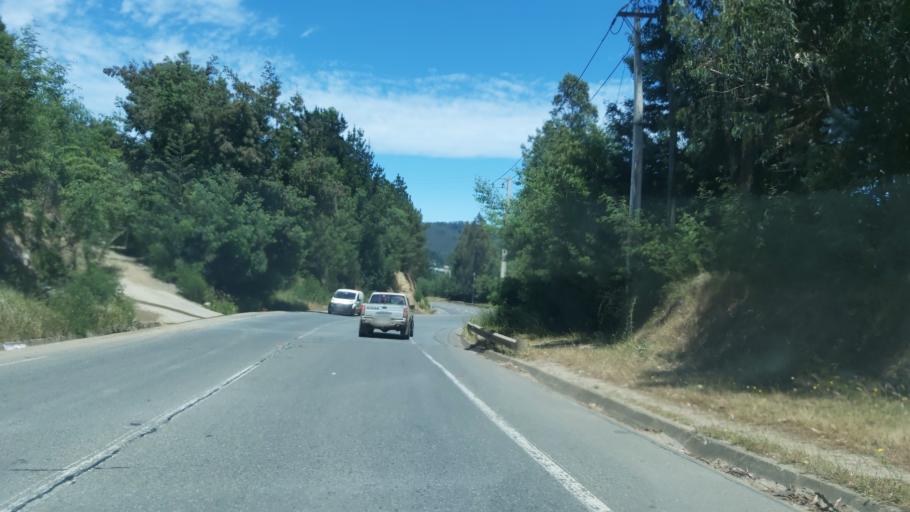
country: CL
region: Maule
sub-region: Provincia de Talca
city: Constitucion
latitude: -35.3308
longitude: -72.3864
